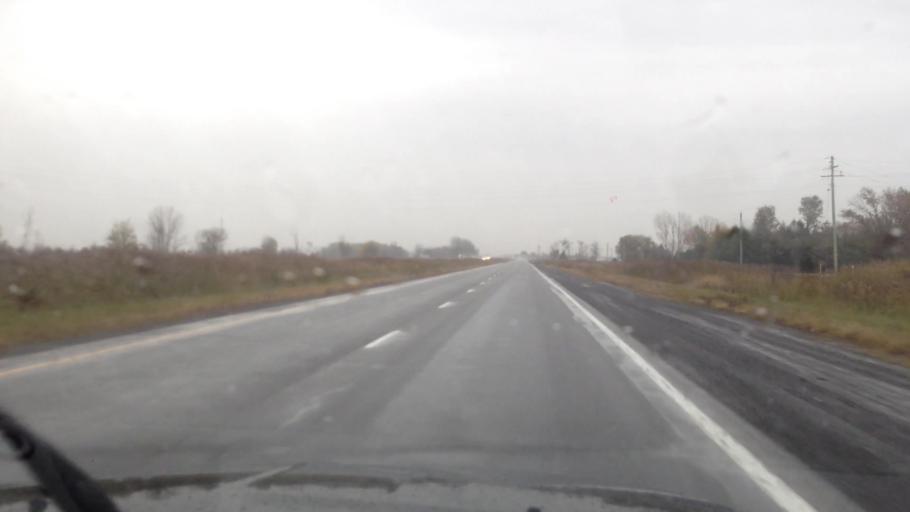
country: CA
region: Ontario
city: Casselman
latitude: 45.3079
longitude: -75.0480
